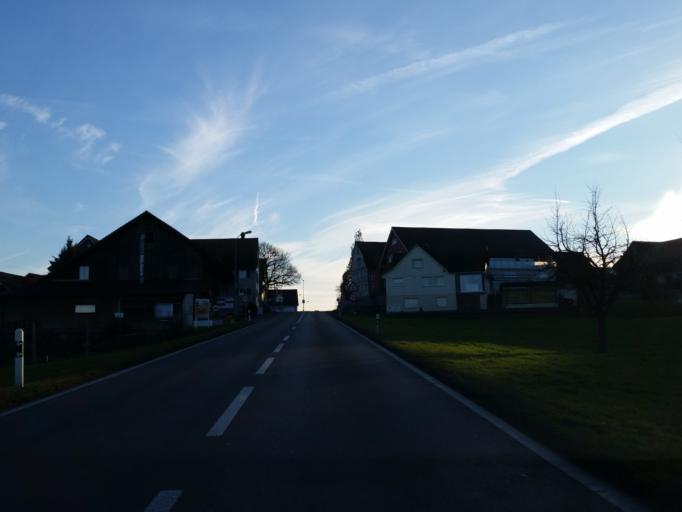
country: CH
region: Thurgau
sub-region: Arbon District
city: Amriswil
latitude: 47.5388
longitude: 9.2665
